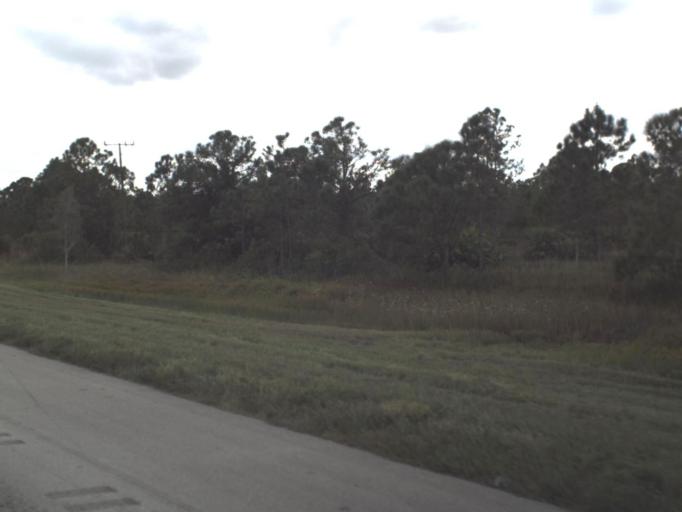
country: US
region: Florida
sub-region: Saint Lucie County
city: River Park
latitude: 27.3494
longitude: -80.3743
